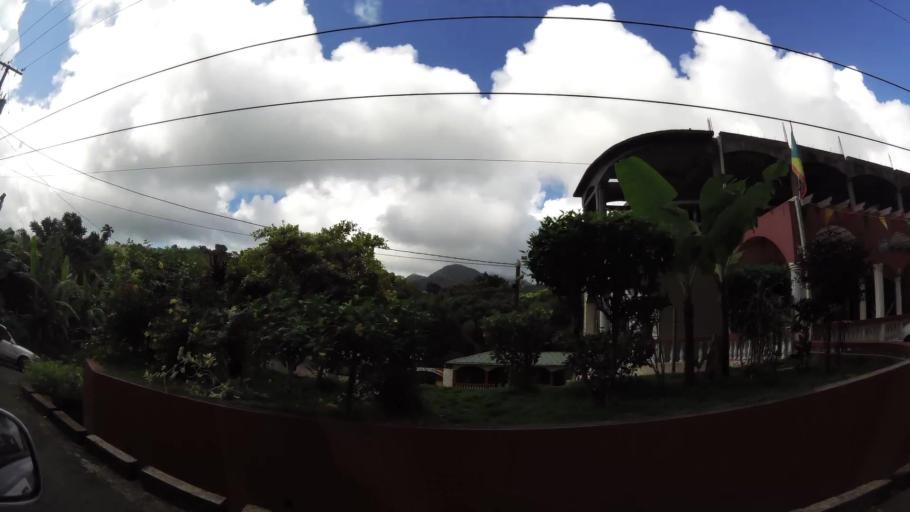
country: GD
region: Saint Andrew
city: Grenville
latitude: 12.1270
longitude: -61.6627
